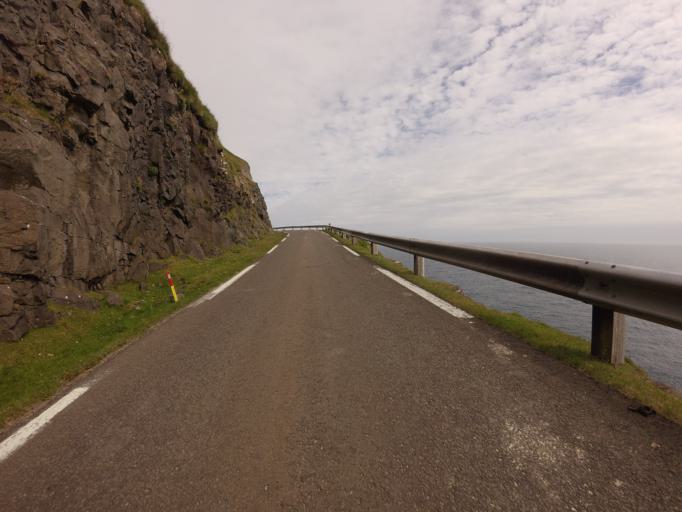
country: FO
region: Sandoy
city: Sandur
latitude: 61.7896
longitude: -6.6590
